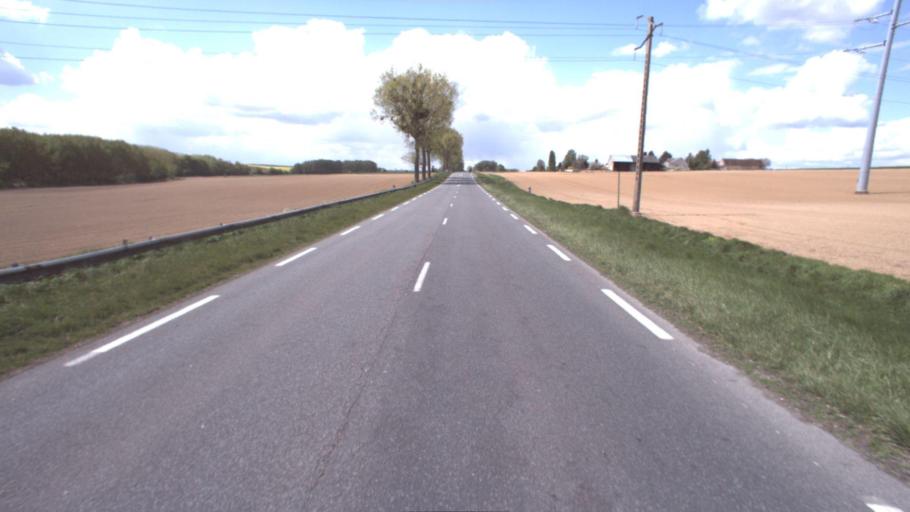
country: FR
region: Ile-de-France
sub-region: Departement de Seine-et-Marne
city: La Ferte-Gaucher
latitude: 48.6933
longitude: 3.3194
